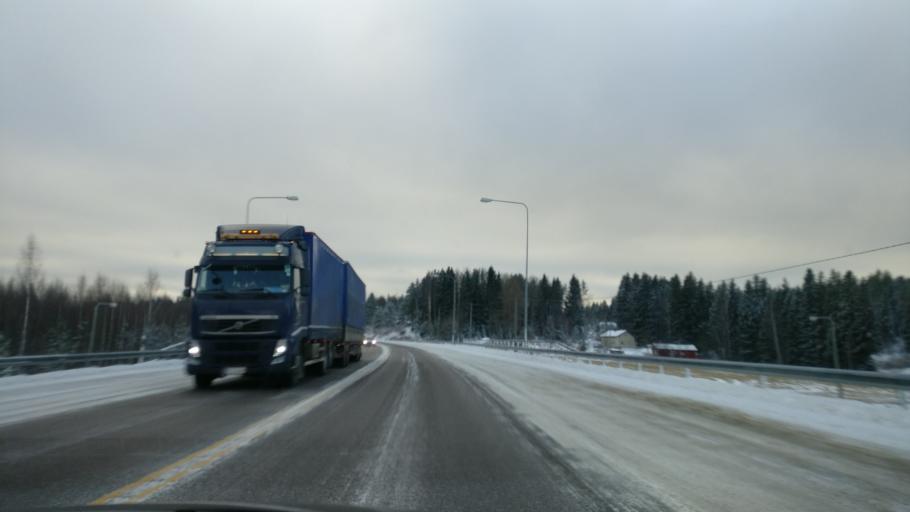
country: FI
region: Paijanne Tavastia
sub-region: Lahti
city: Heinola
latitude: 61.3324
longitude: 26.1652
